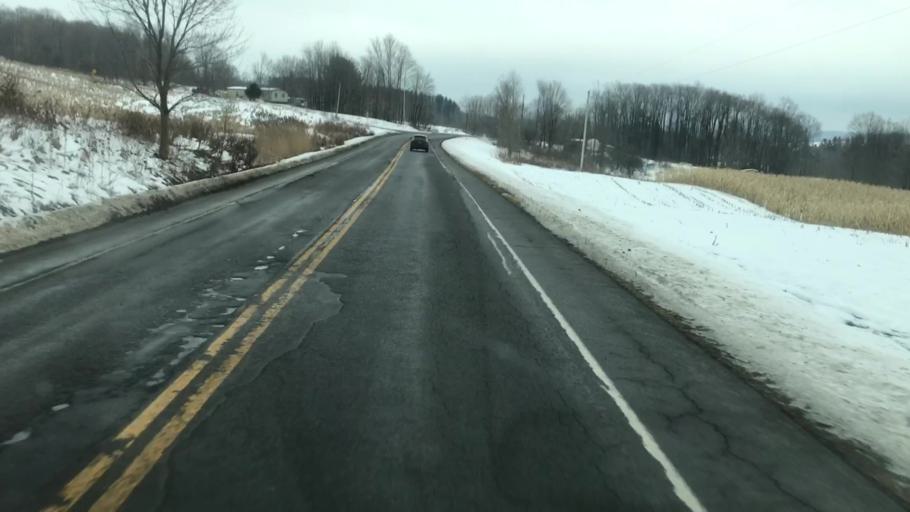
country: US
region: New York
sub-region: Cayuga County
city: Moravia
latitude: 42.7366
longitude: -76.3151
